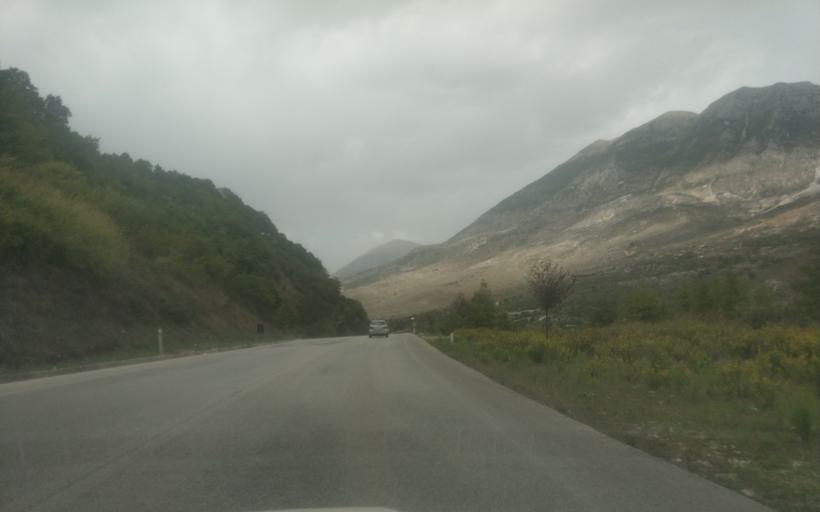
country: AL
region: Gjirokaster
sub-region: Rrethi i Gjirokastres
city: Picar
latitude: 40.2251
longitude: 20.0860
